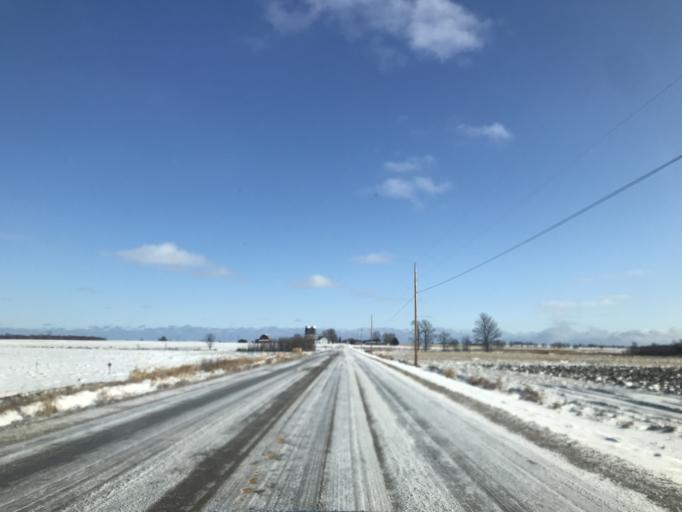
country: US
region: Wisconsin
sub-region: Kewaunee County
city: Luxemburg
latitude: 44.6976
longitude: -87.6079
